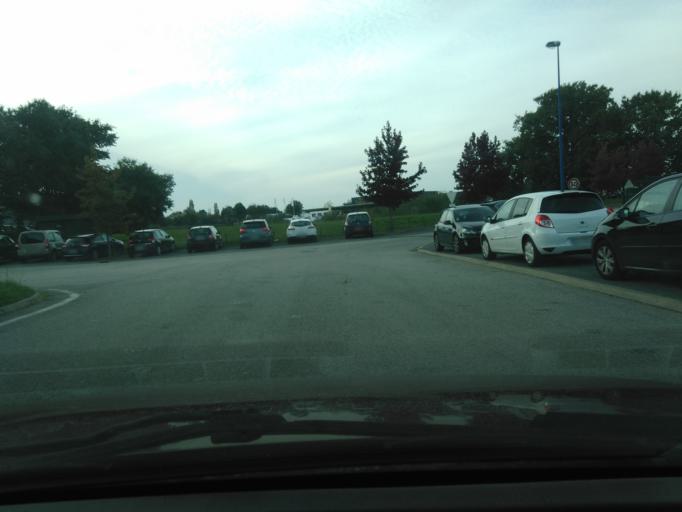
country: FR
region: Pays de la Loire
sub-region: Departement de la Vendee
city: Mouilleron-le-Captif
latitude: 46.7234
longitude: -1.4265
